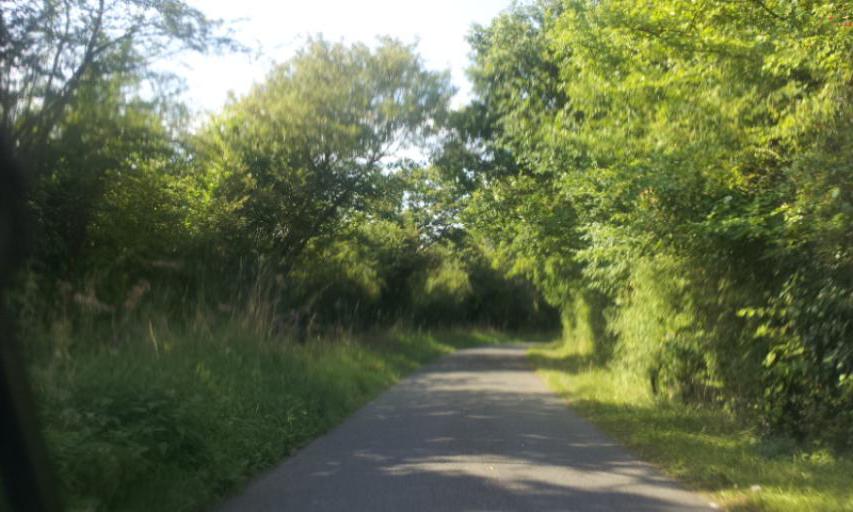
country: GB
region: England
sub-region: Kent
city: Yalding
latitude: 51.2001
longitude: 0.4398
